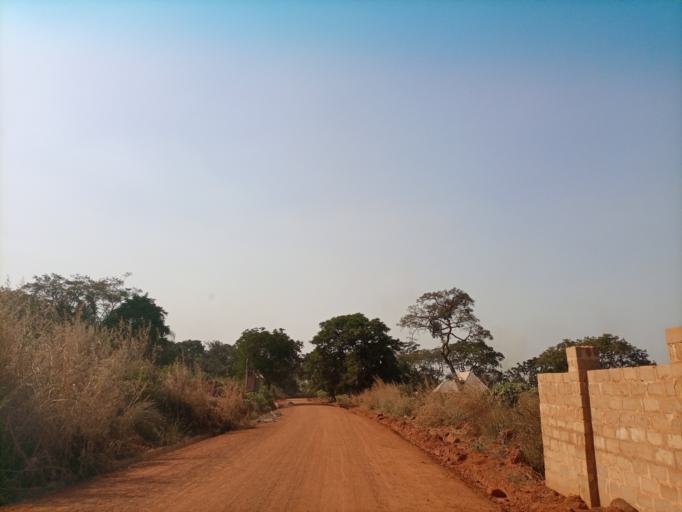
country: NG
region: Enugu
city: Aku
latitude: 6.7042
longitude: 7.3141
